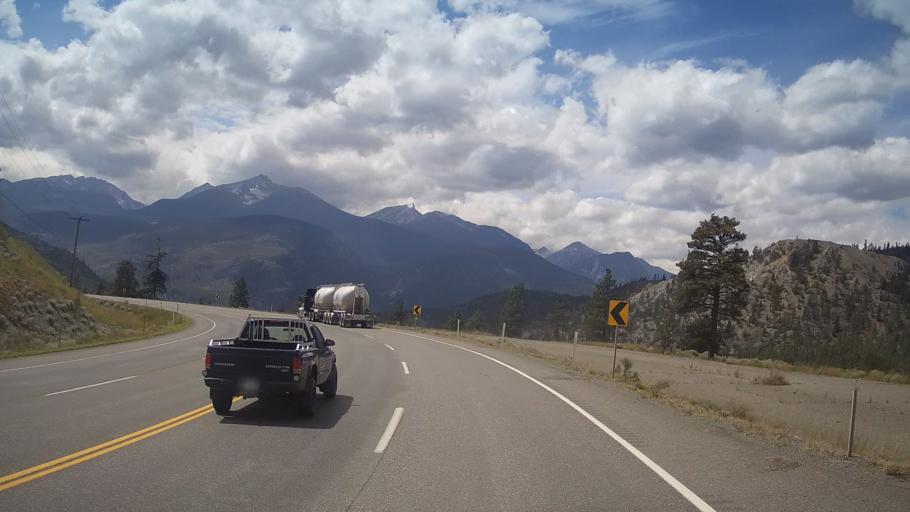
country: CA
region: British Columbia
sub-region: Thompson-Nicola Regional District
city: Ashcroft
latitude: 50.2598
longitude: -121.5394
